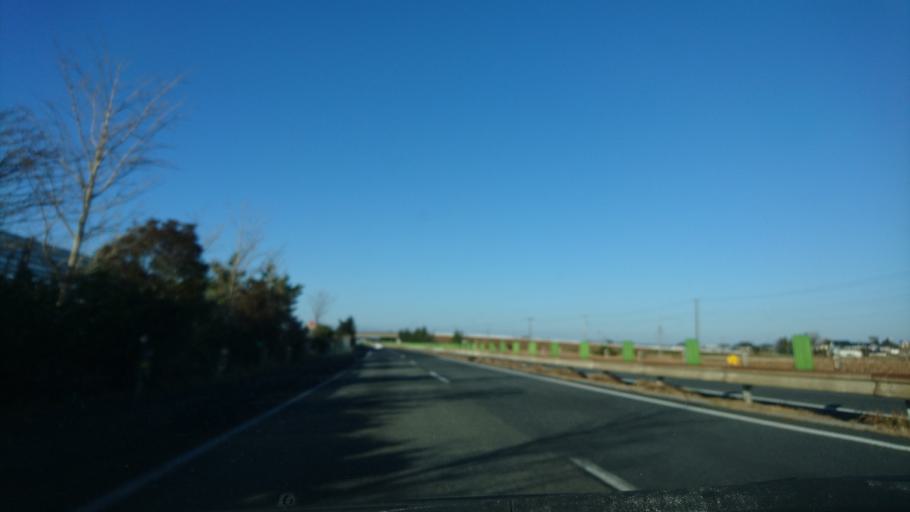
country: JP
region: Miyagi
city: Furukawa
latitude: 38.5557
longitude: 140.9310
